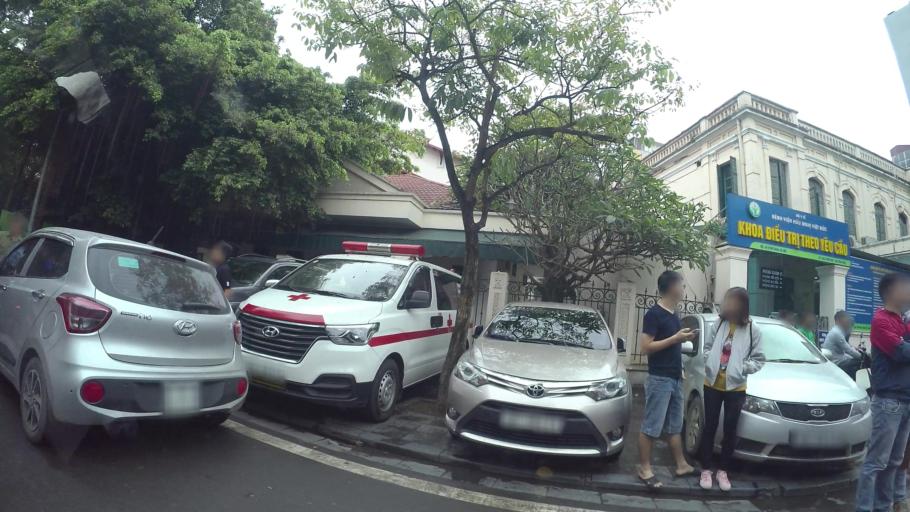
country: VN
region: Ha Noi
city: Hoan Kiem
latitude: 21.0299
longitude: 105.8476
